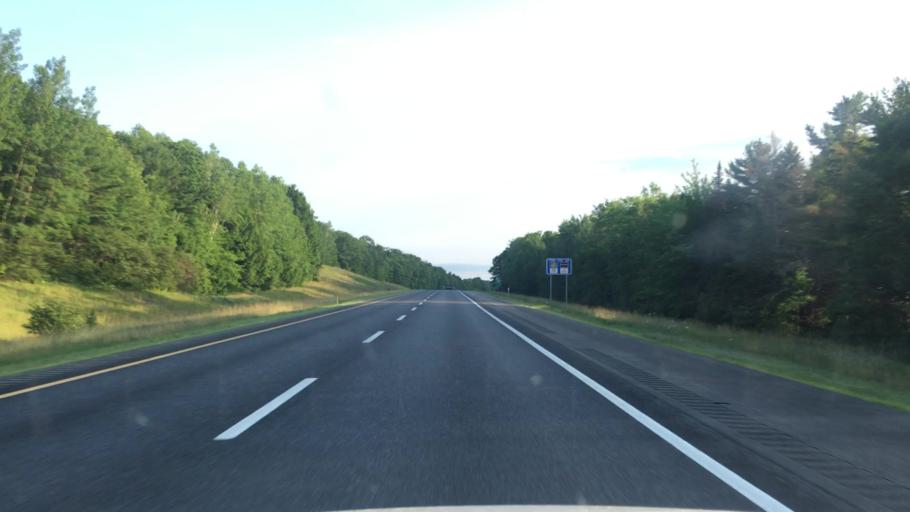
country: US
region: Maine
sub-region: Sagadahoc County
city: Topsham
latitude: 43.9650
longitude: -69.9572
